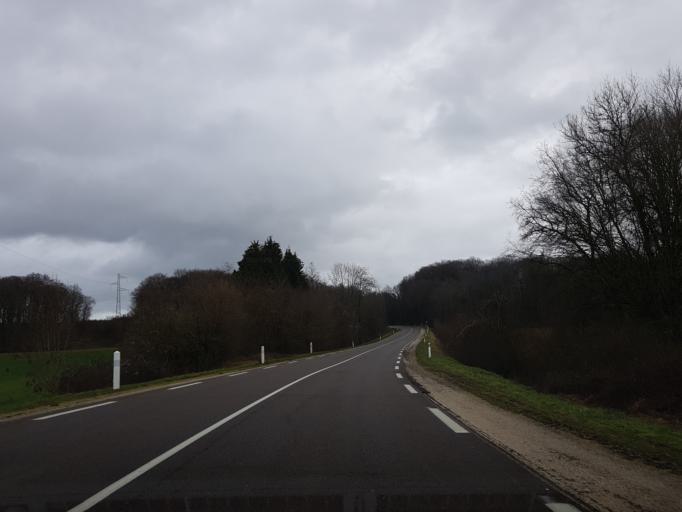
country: FR
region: Franche-Comte
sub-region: Departement de la Haute-Saone
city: Scey-sur-Saone-et-Saint-Albin
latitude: 47.7079
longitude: 5.9272
